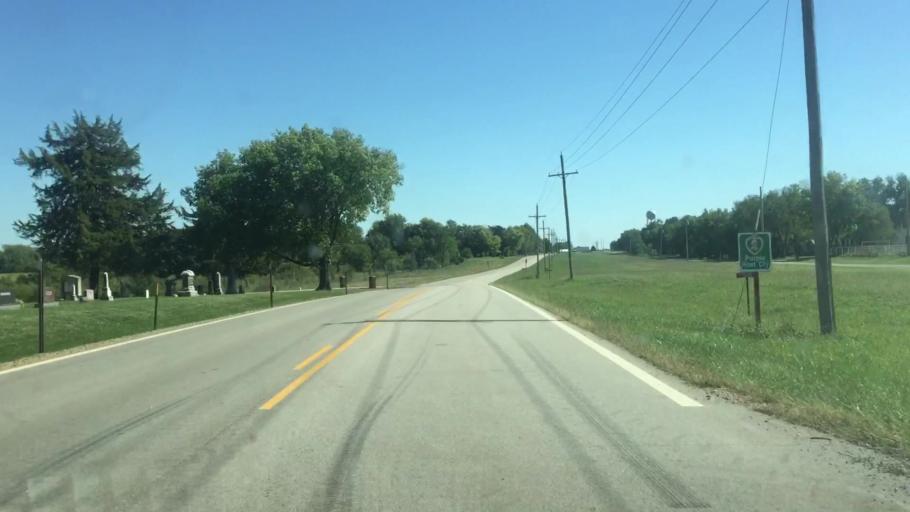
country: US
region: Kansas
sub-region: Jackson County
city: Holton
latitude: 39.6081
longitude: -95.7232
